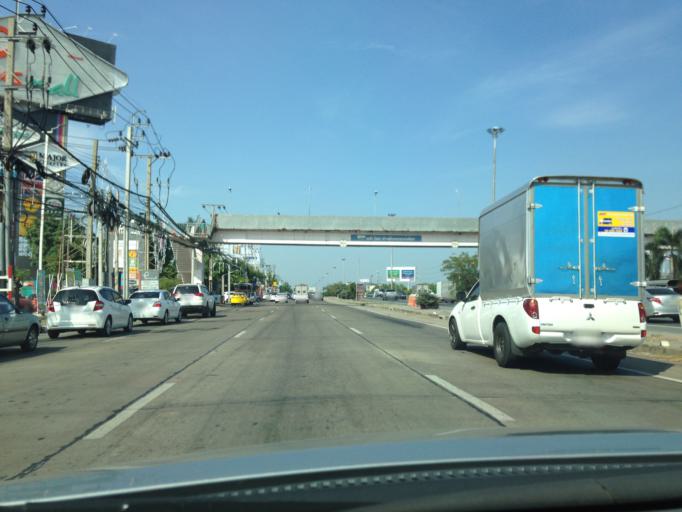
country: TH
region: Nonthaburi
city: Bang Yai
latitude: 13.8244
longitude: 100.4124
